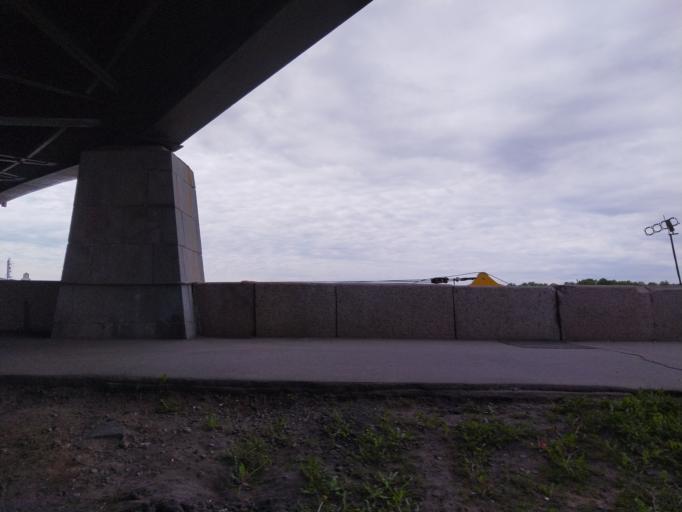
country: RU
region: Leningrad
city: Finlyandskiy
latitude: 59.9470
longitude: 30.4064
